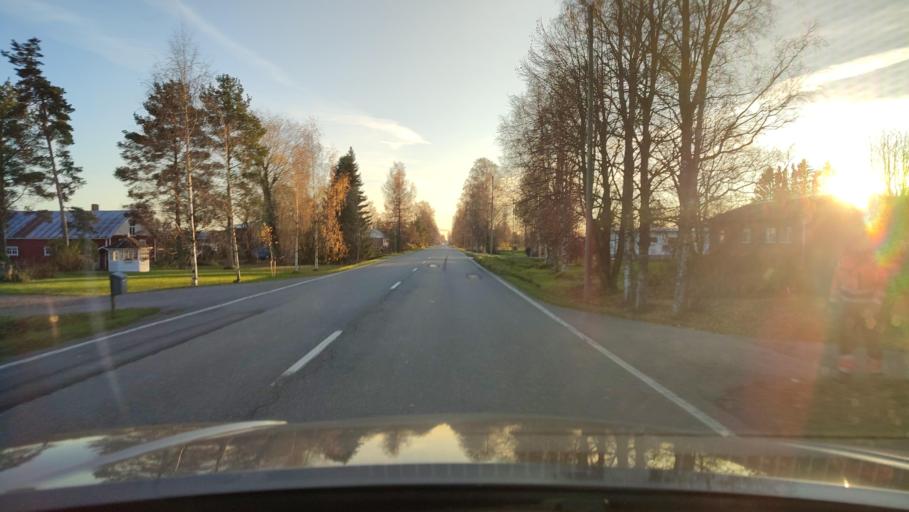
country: FI
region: Ostrobothnia
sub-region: Sydosterbotten
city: Naerpes
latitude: 62.5541
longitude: 21.4060
